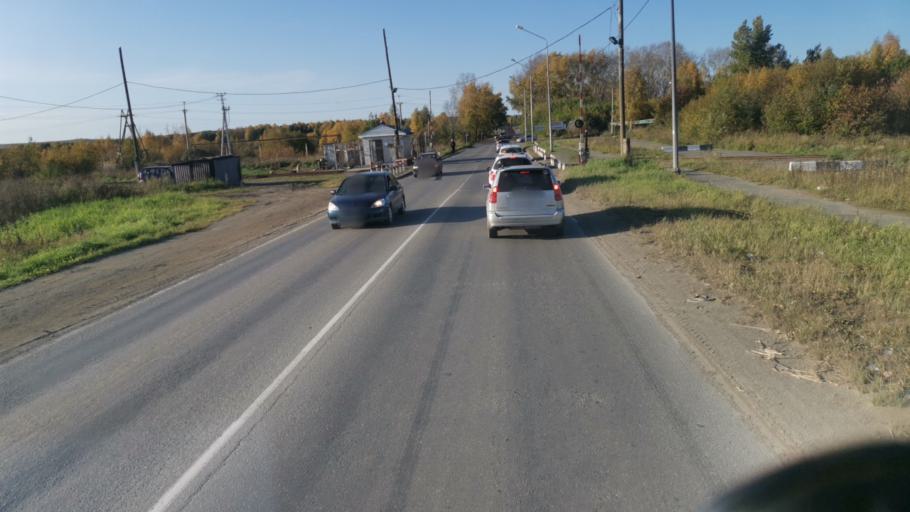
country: RU
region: Sverdlovsk
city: Nizhniy Tagil
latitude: 57.9426
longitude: 59.9224
